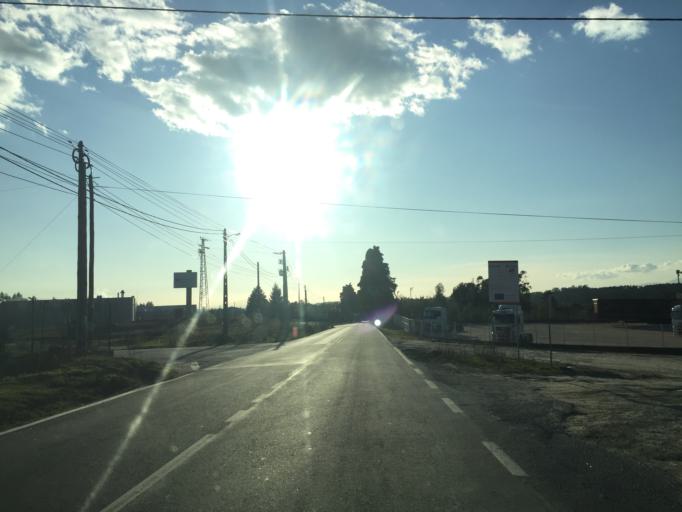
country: PT
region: Viseu
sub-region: Nelas
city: Nelas
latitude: 40.5186
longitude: -7.8740
